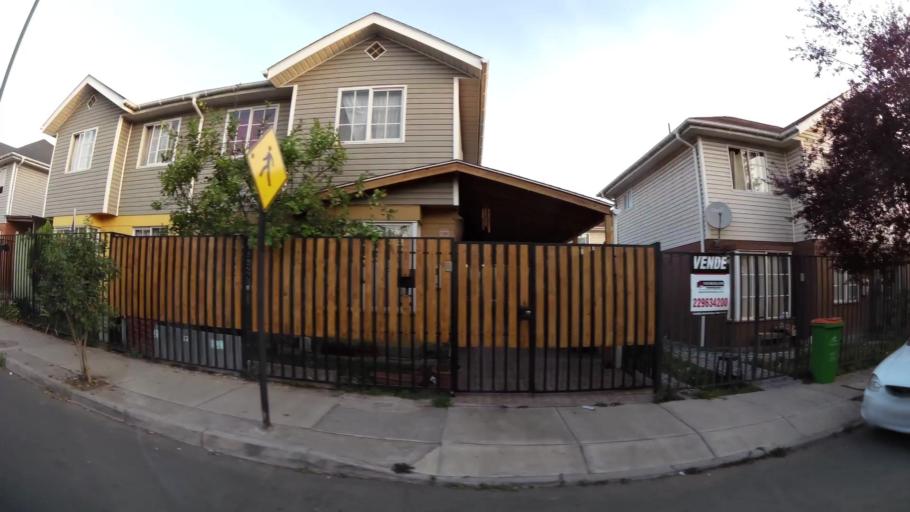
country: CL
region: Santiago Metropolitan
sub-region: Provincia de Cordillera
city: Puente Alto
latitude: -33.5983
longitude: -70.5858
